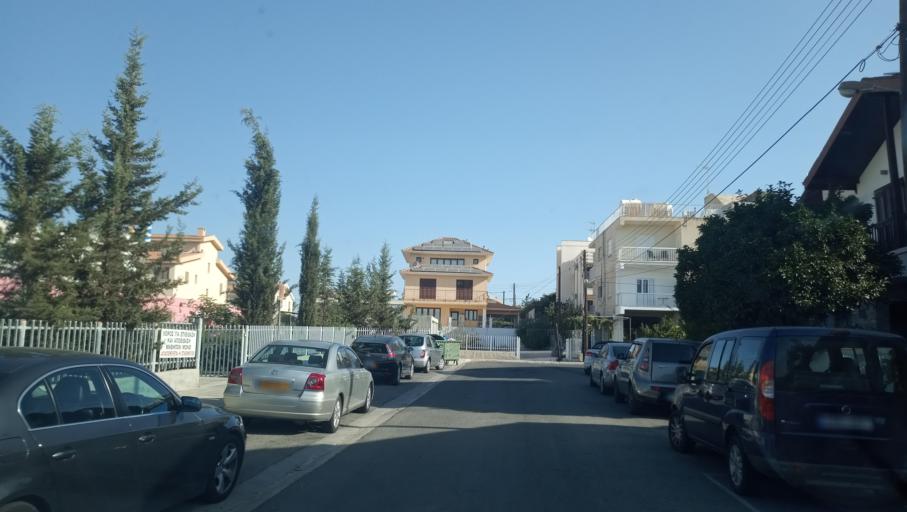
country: CY
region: Lefkosia
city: Nicosia
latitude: 35.1465
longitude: 33.3986
